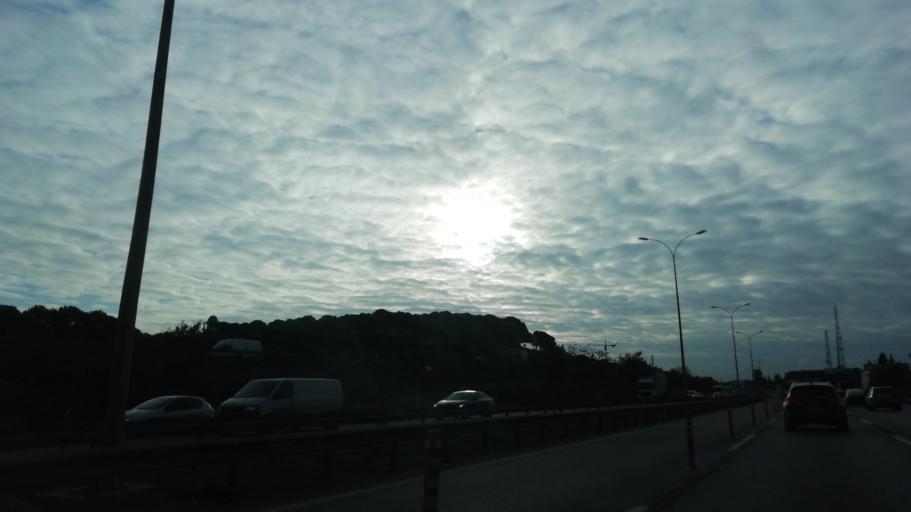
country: TR
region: Kocaeli
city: Balcik
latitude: 40.8931
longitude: 29.3706
